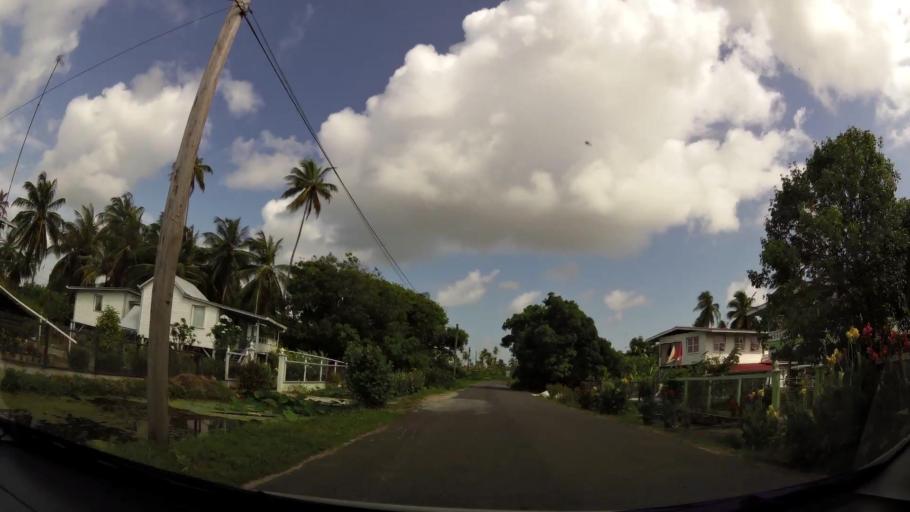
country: GY
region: Demerara-Mahaica
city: Mahaica Village
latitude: 6.7159
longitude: -57.9323
